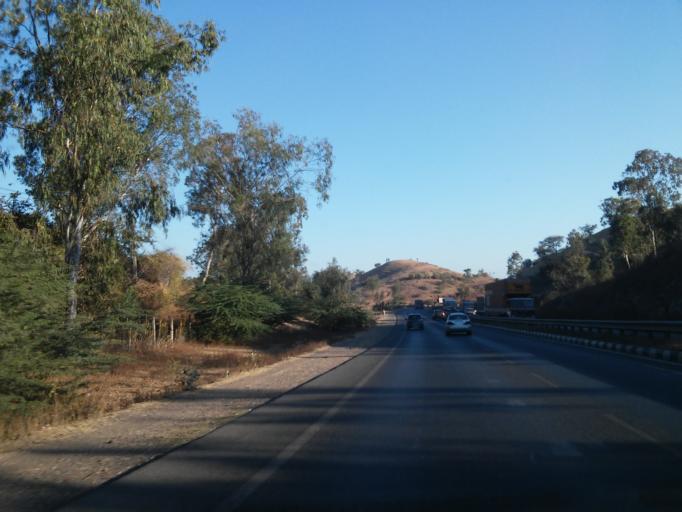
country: IN
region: Rajasthan
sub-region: Dungarpur
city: Dungarpur
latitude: 23.9043
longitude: 73.5469
